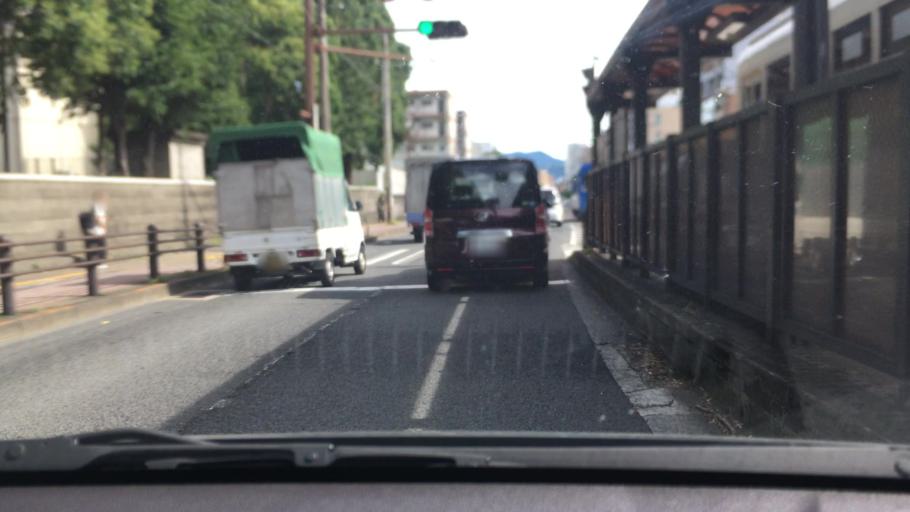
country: JP
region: Nagasaki
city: Obita
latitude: 32.7851
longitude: 129.8625
